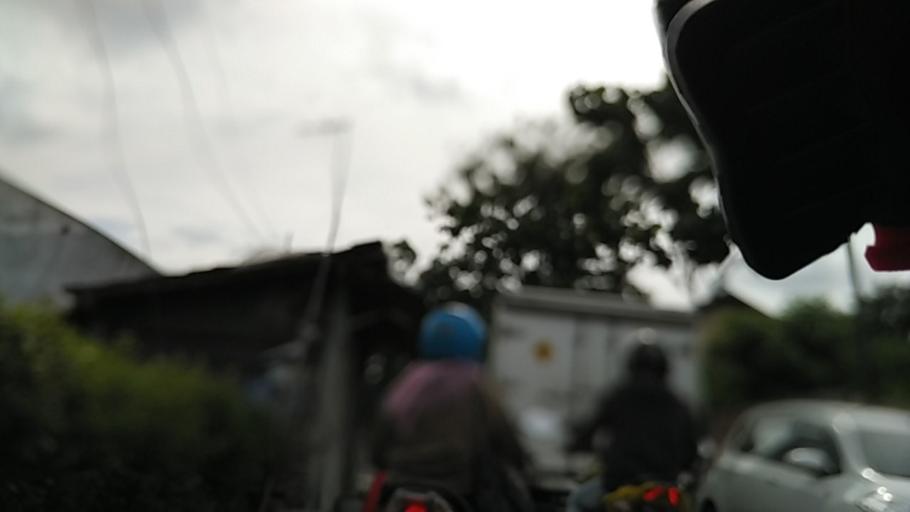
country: ID
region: Central Java
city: Semarang
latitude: -6.9973
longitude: 110.4116
